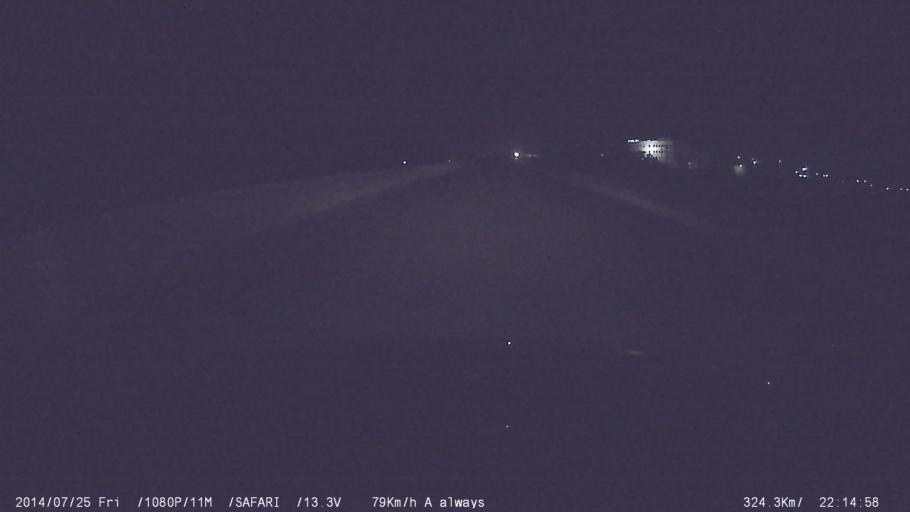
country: IN
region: Tamil Nadu
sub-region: Tiruppur
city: Avinashi
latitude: 11.1370
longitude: 77.2030
